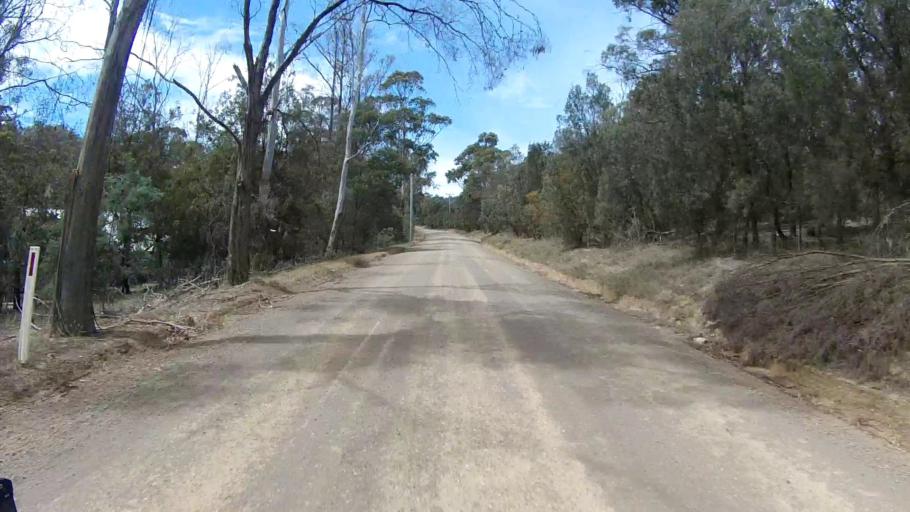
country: AU
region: Tasmania
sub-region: Sorell
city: Sorell
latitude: -42.8013
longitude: 147.6671
